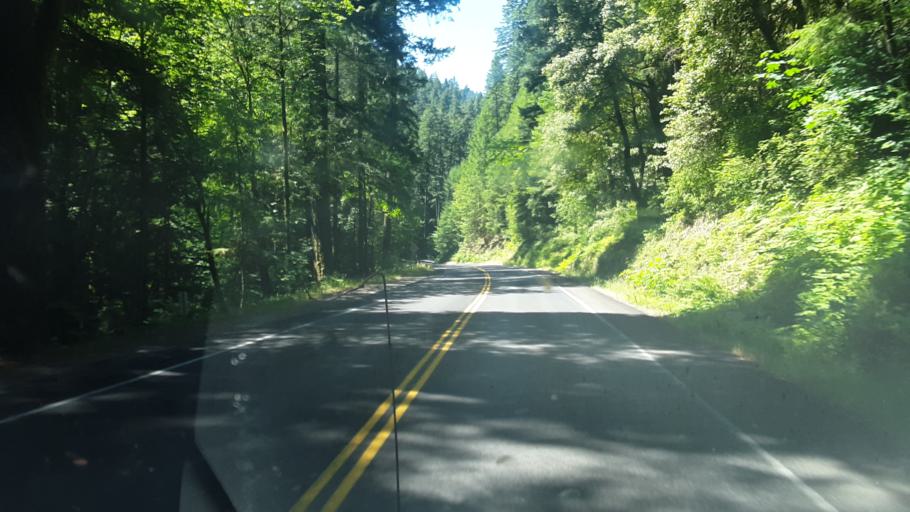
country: US
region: Oregon
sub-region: Josephine County
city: Cave Junction
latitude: 41.9323
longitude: -123.7563
